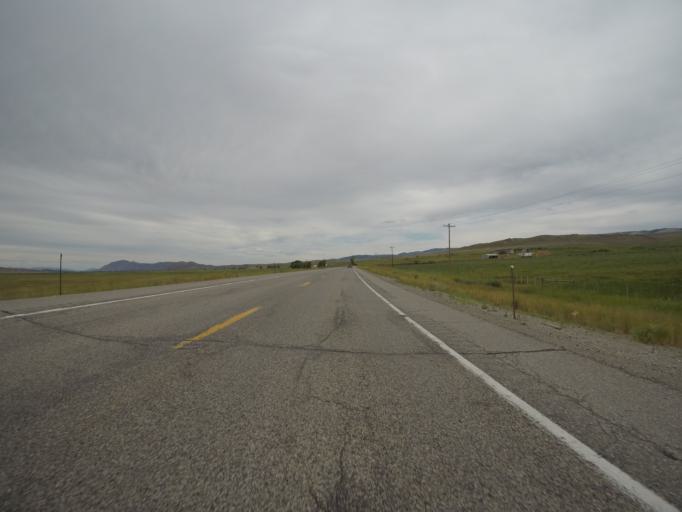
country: US
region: Utah
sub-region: Rich County
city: Randolph
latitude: 42.0172
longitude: -110.9361
